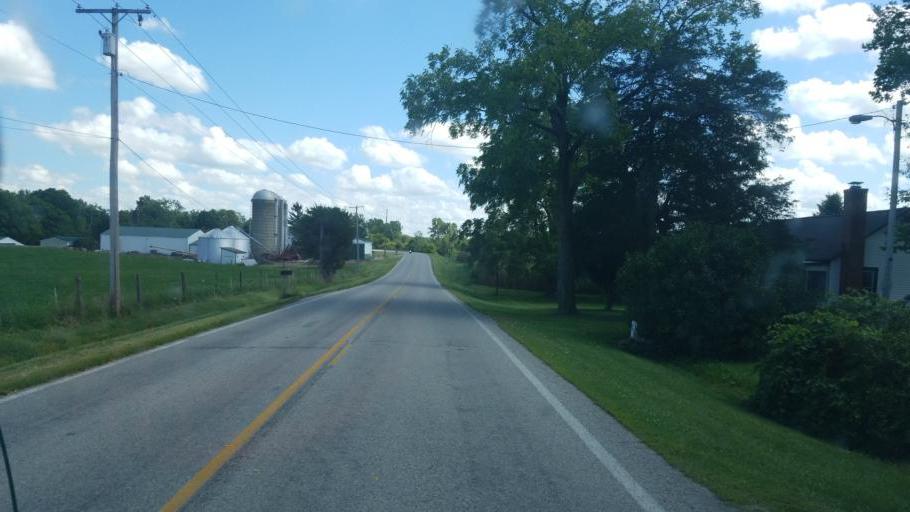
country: US
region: Ohio
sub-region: Marion County
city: Prospect
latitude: 40.3266
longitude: -83.1954
